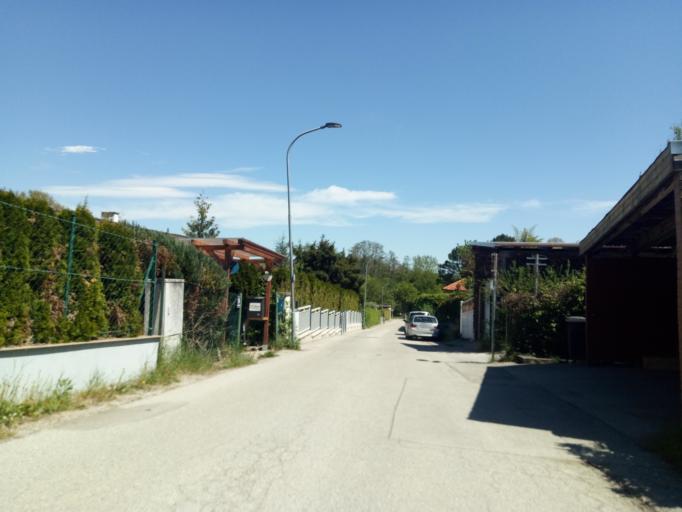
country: AT
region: Lower Austria
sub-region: Politischer Bezirk Modling
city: Kaltenleutgeben
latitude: 48.1255
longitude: 16.1864
